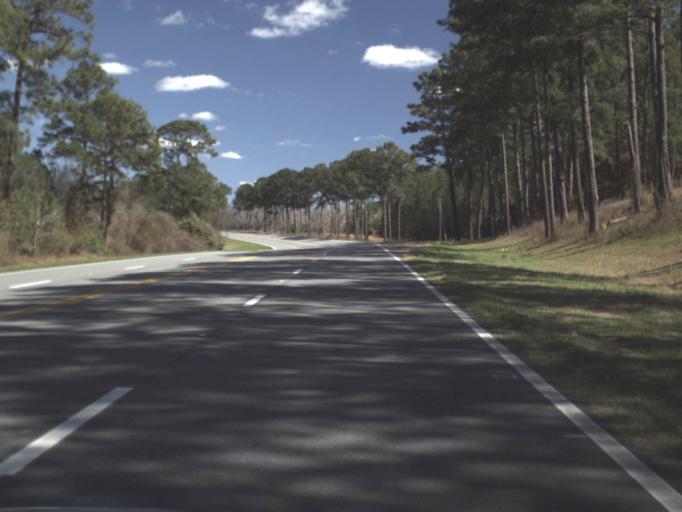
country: US
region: Florida
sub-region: Gadsden County
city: Chattahoochee
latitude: 30.7007
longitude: -84.8116
